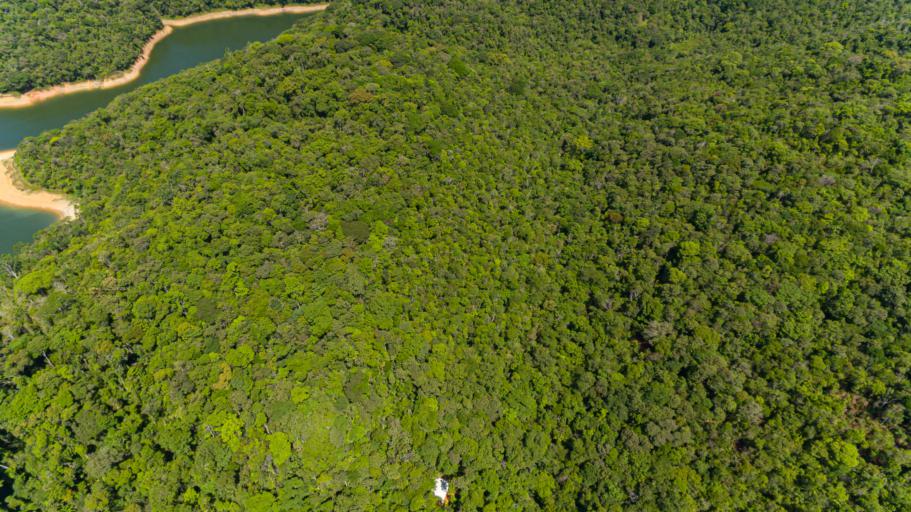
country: BR
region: Sao Paulo
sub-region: Juquitiba
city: Juquitiba
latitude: -24.0249
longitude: -47.2498
